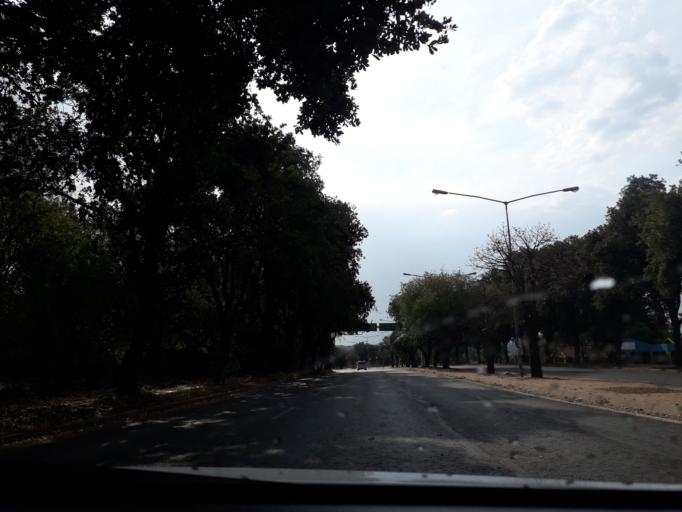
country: ZA
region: Gauteng
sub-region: City of Johannesburg Metropolitan Municipality
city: Modderfontein
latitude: -26.1017
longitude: 28.2291
